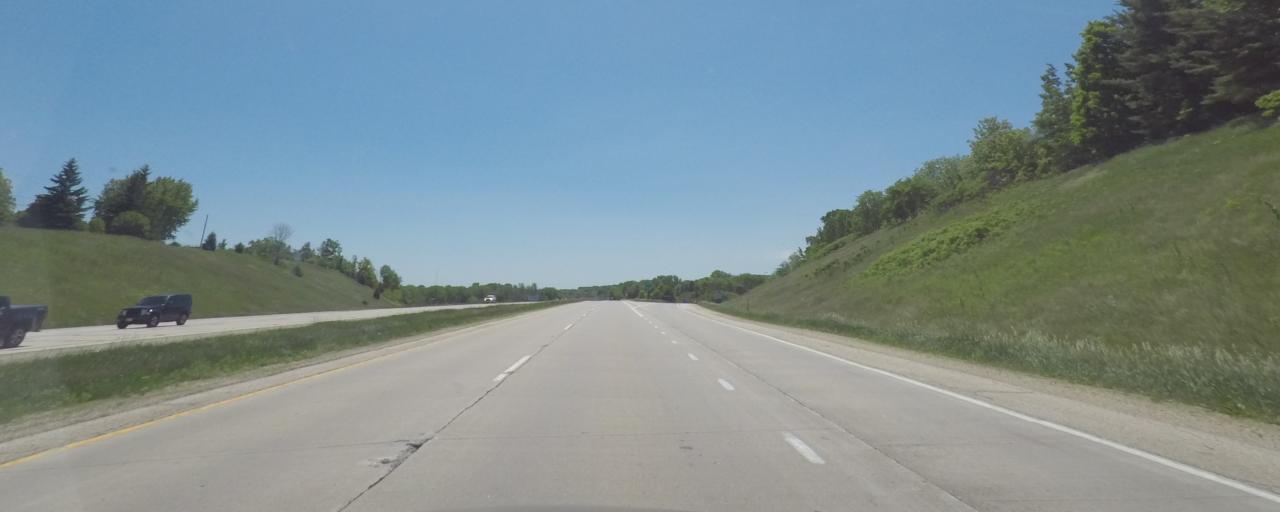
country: US
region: Wisconsin
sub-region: Washington County
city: West Bend
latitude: 43.4310
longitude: -88.2089
